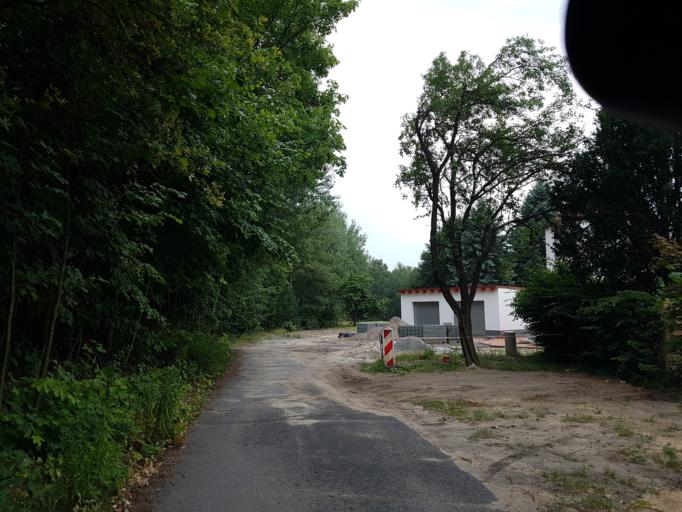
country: DE
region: Brandenburg
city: Sallgast
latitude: 51.5797
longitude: 13.8532
